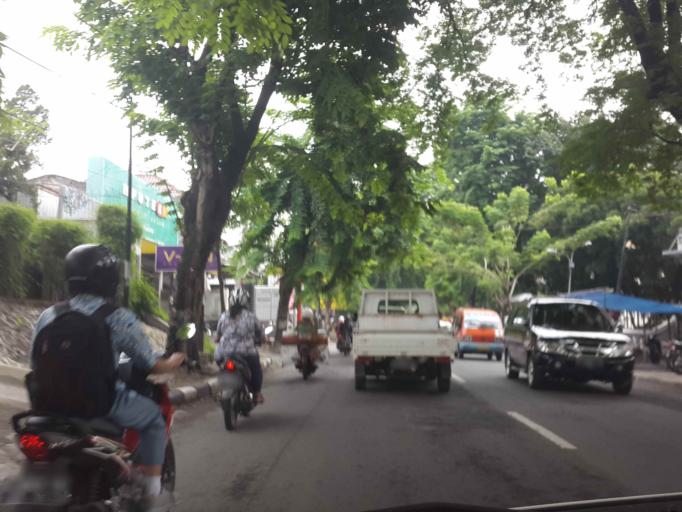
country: ID
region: Central Java
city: Semarang
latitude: -7.0027
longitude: 110.4253
